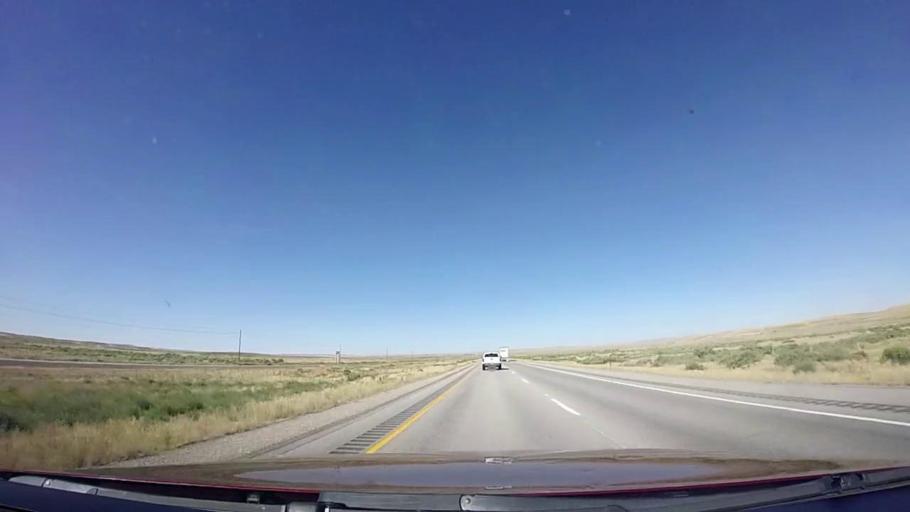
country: US
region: Wyoming
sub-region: Carbon County
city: Rawlins
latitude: 41.7826
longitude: -107.4243
